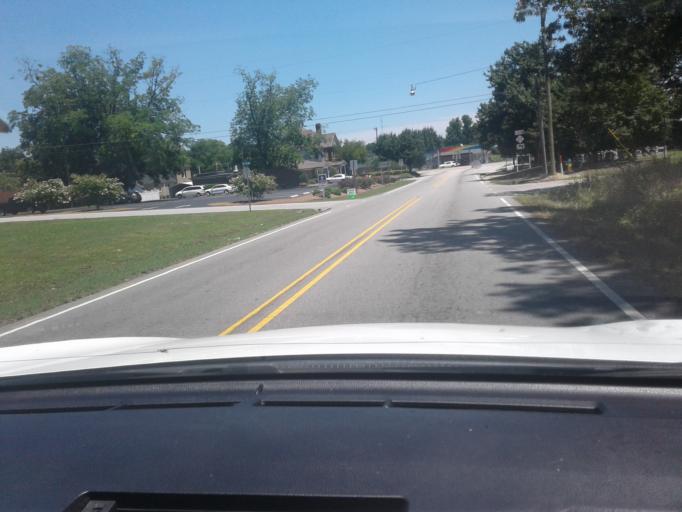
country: US
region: North Carolina
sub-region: Harnett County
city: Lillington
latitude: 35.3931
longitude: -78.8204
